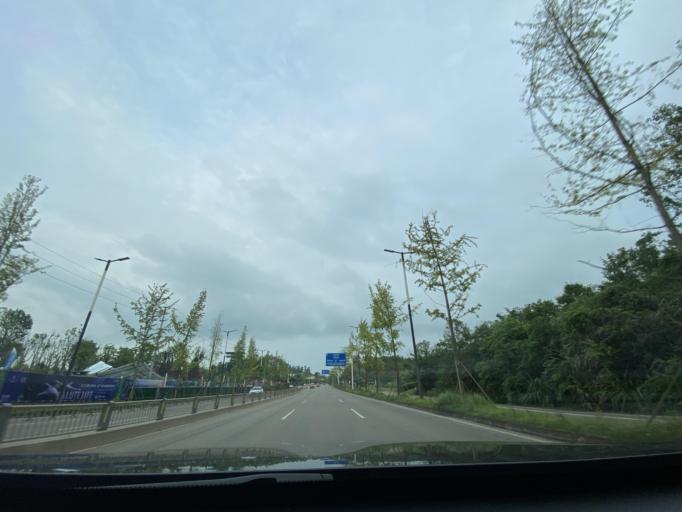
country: CN
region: Sichuan
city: Jiancheng
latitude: 30.4946
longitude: 104.4601
